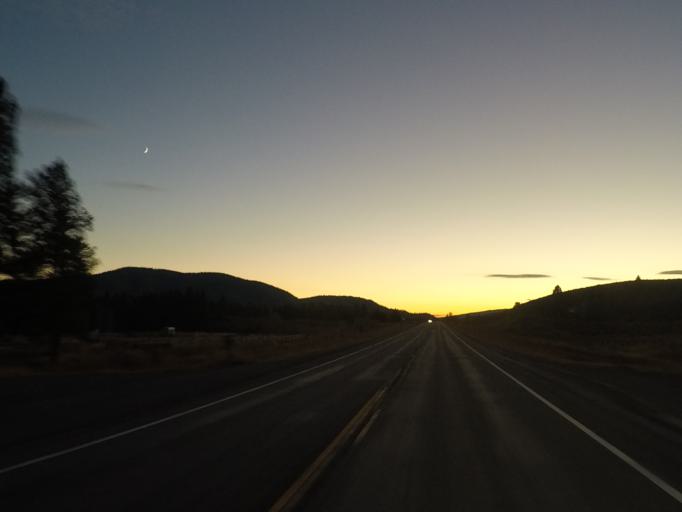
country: US
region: Montana
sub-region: Missoula County
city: Seeley Lake
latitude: 47.0426
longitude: -113.2152
